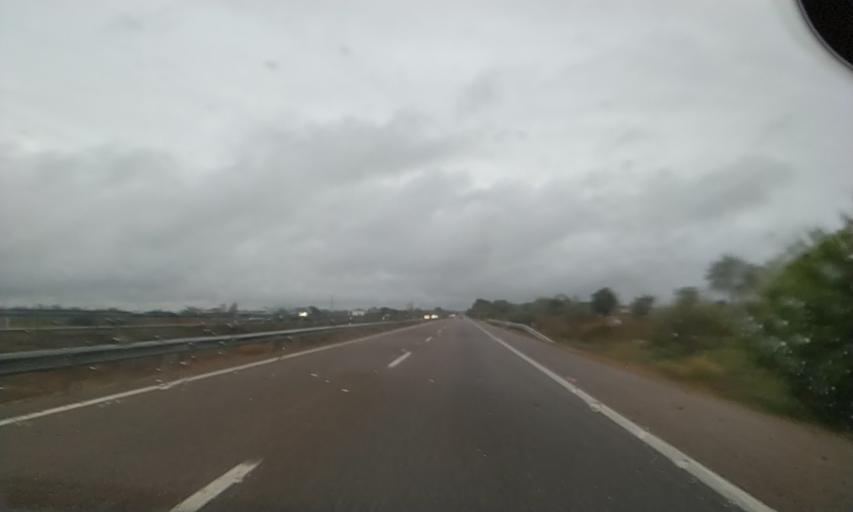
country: ES
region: Extremadura
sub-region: Provincia de Badajoz
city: Arroyo de San Servan
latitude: 38.8837
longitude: -6.4387
